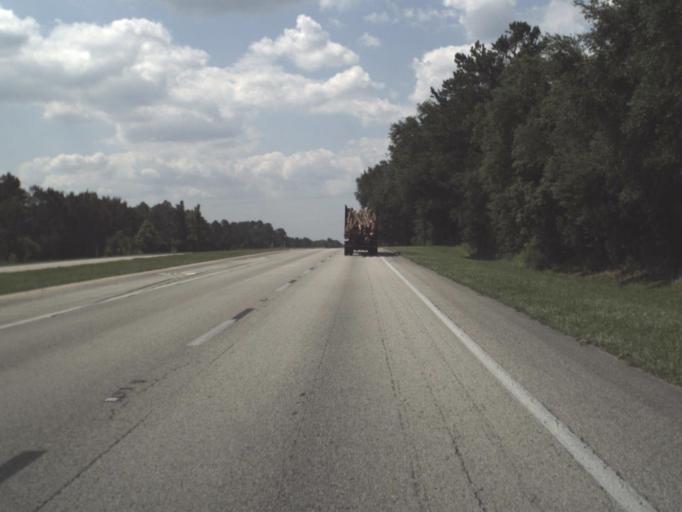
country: US
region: Florida
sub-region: Alachua County
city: Waldo
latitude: 29.6956
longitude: -82.1305
